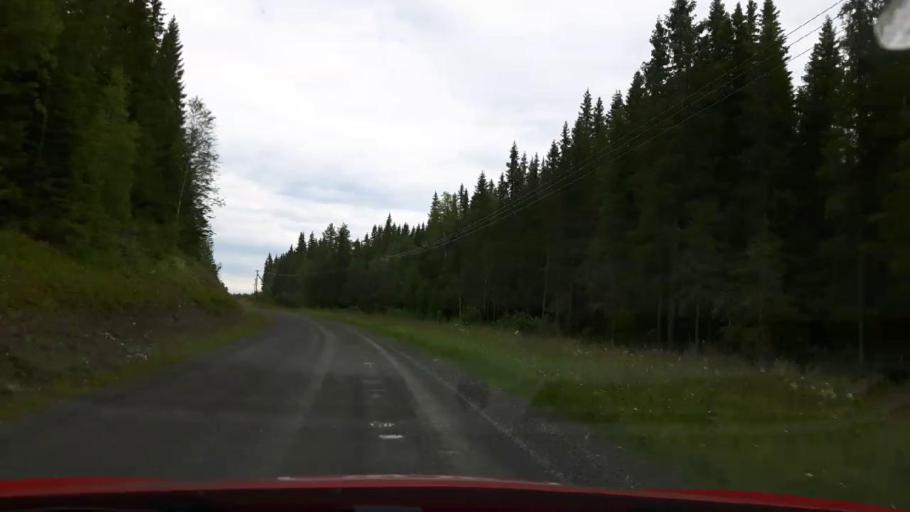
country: SE
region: Jaemtland
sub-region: Stroemsunds Kommun
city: Stroemsund
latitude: 63.4816
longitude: 15.3046
